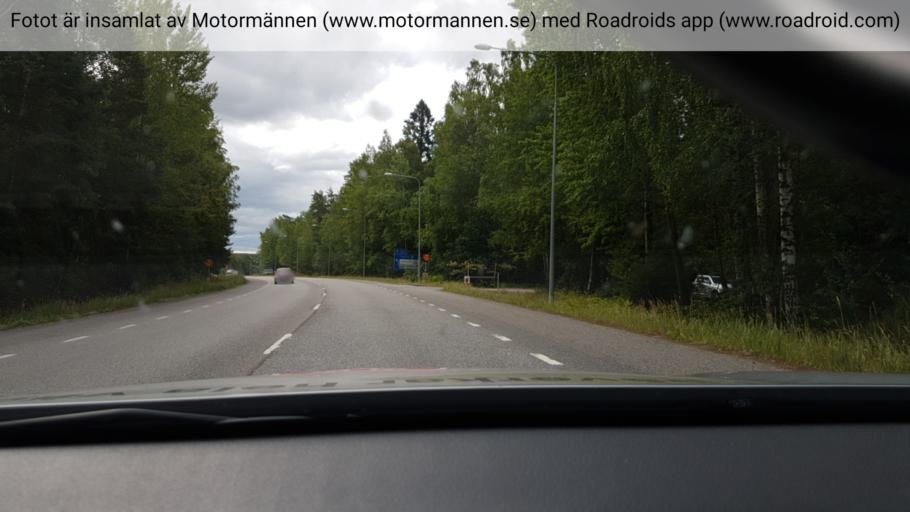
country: SE
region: Stockholm
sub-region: Nacka Kommun
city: Alta
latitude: 59.2355
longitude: 18.1902
